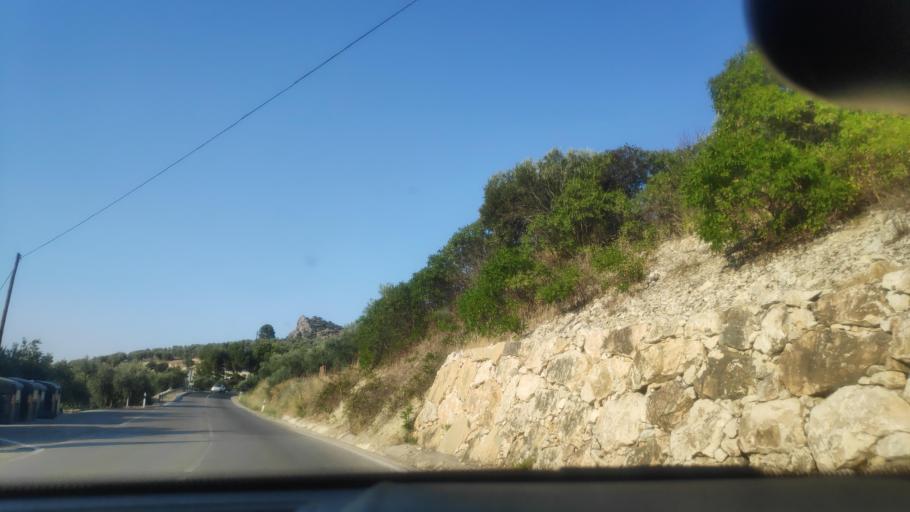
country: ES
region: Andalusia
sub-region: Provincia de Jaen
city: Jaen
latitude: 37.7465
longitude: -3.7898
